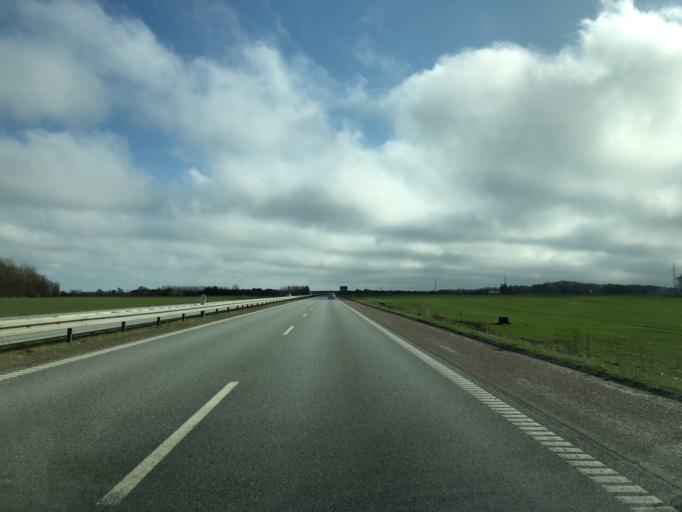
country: DK
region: North Denmark
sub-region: Hjorring Kommune
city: Hjorring
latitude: 57.4398
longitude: 10.0378
